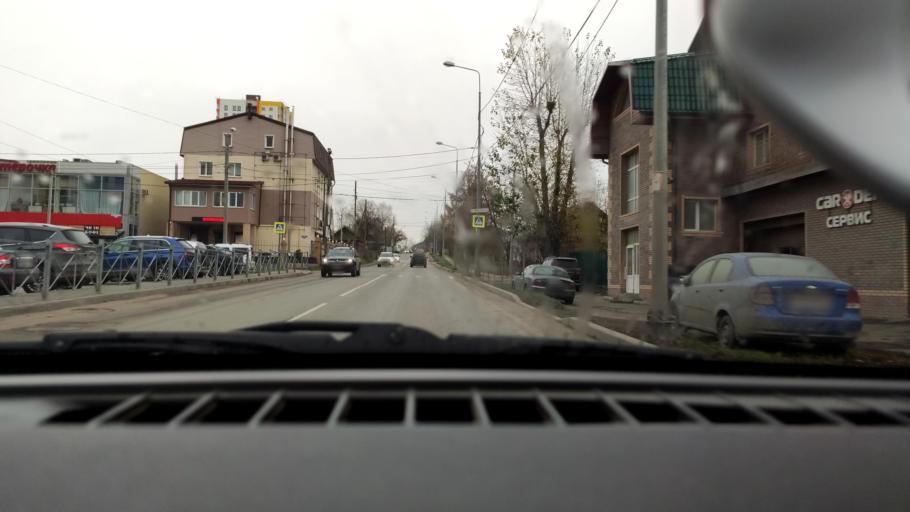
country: RU
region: Perm
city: Kondratovo
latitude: 57.9667
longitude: 56.1518
